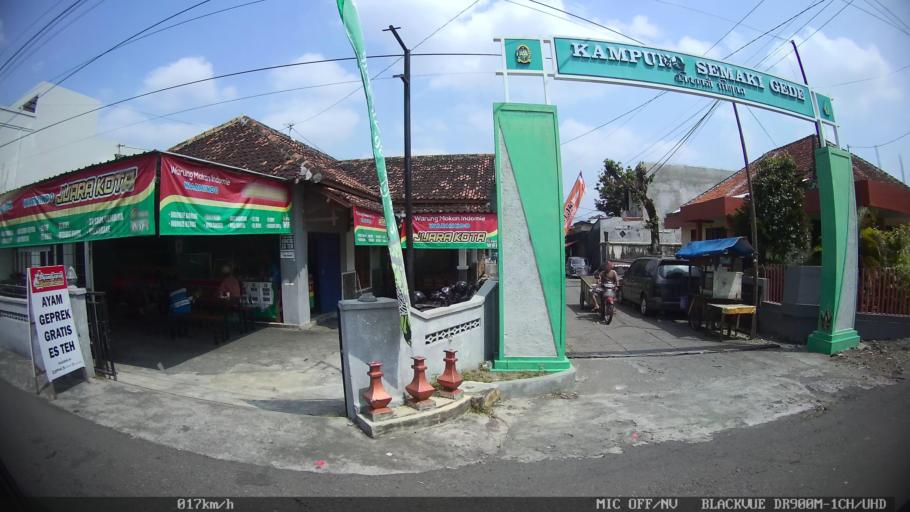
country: ID
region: Daerah Istimewa Yogyakarta
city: Yogyakarta
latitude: -7.8002
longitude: 110.3876
